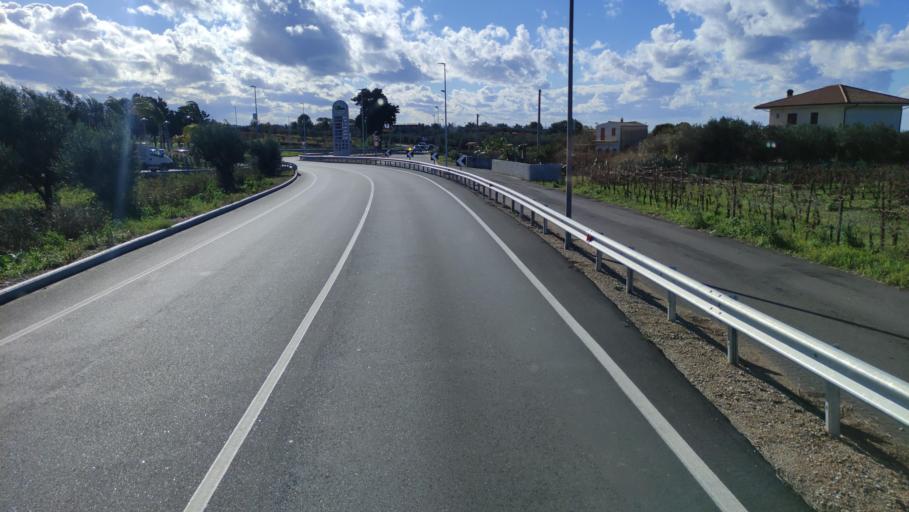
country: IT
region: Calabria
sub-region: Provincia di Catanzaro
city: Santa Eufemia Lamezia
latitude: 38.9253
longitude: 16.2833
